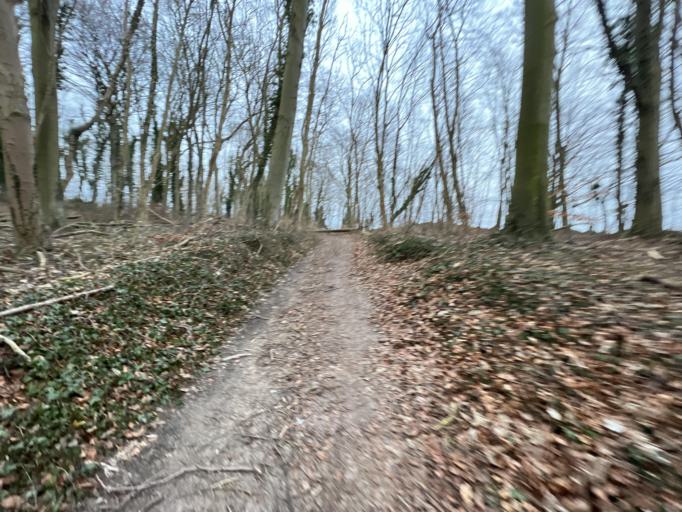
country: DE
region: Mecklenburg-Vorpommern
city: Ostseebad Gohren
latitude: 54.3405
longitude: 13.7599
